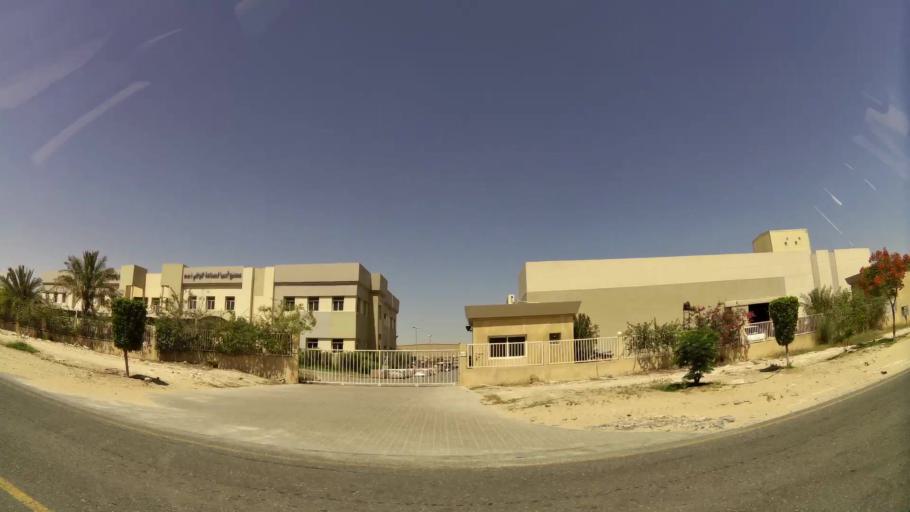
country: AE
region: Dubai
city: Dubai
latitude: 24.9829
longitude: 55.2071
